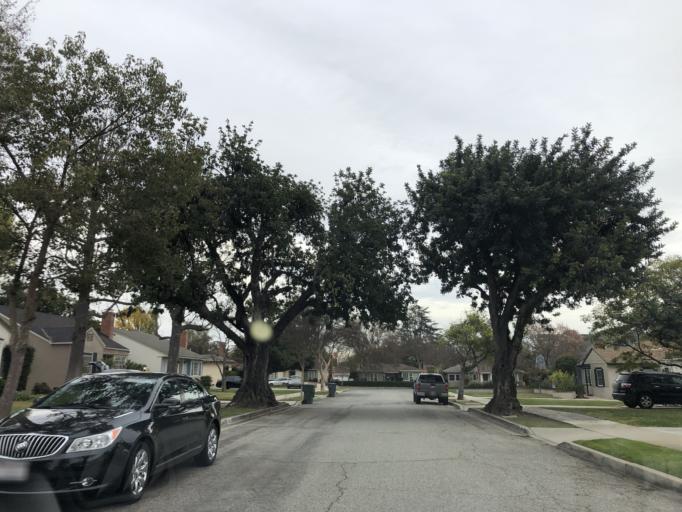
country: US
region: California
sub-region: Los Angeles County
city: San Marino
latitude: 34.1130
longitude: -118.1054
